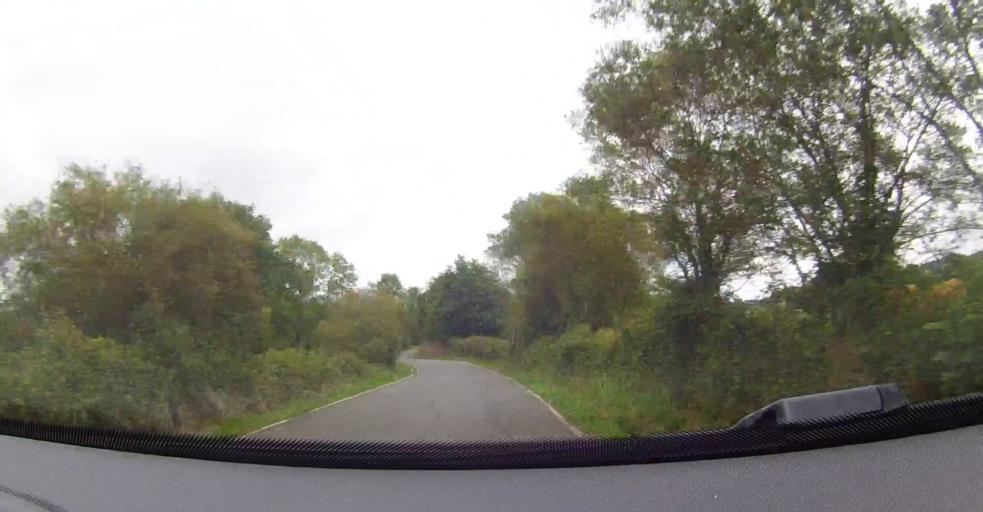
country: ES
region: Basque Country
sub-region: Bizkaia
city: Urrestieta
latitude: 43.2322
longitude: -3.1884
